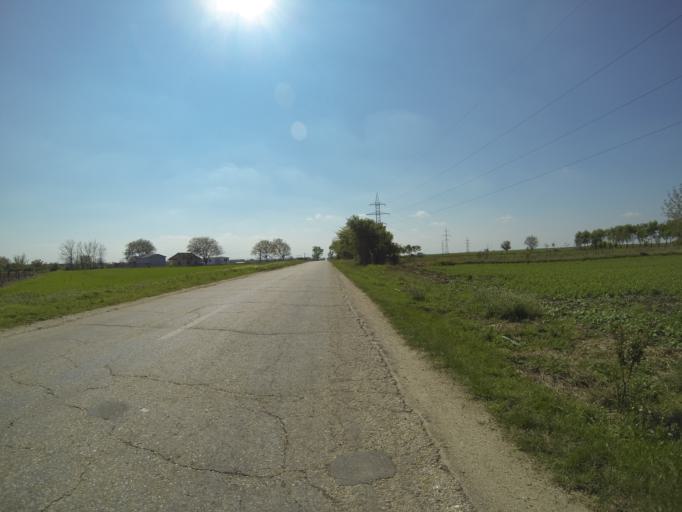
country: RO
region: Dolj
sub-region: Comuna Unirea
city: Unirea
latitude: 44.1698
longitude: 23.1765
